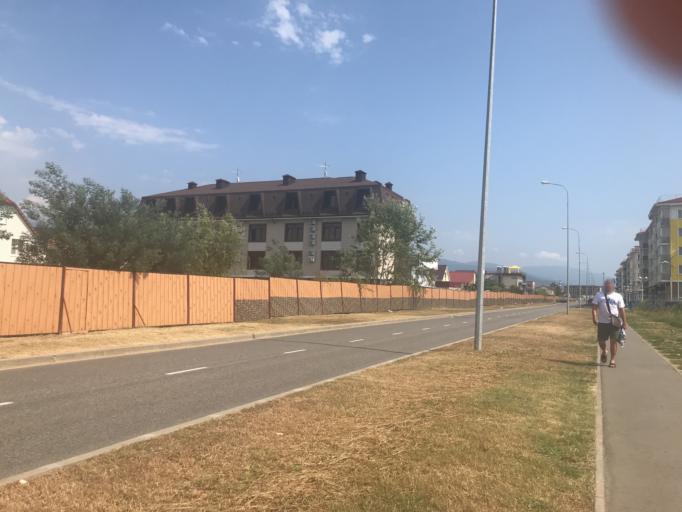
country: RU
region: Krasnodarskiy
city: Vysokoye
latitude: 43.4045
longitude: 39.9820
